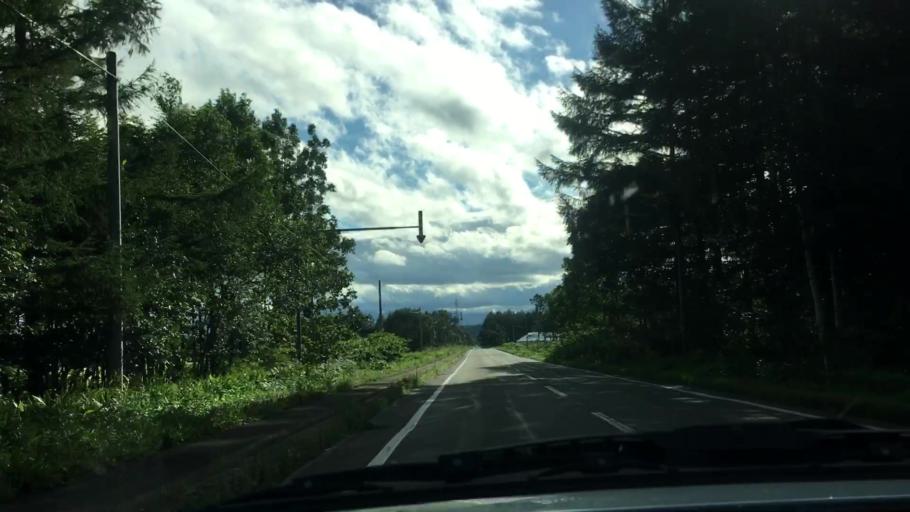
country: JP
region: Hokkaido
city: Otofuke
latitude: 43.1843
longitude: 143.0198
